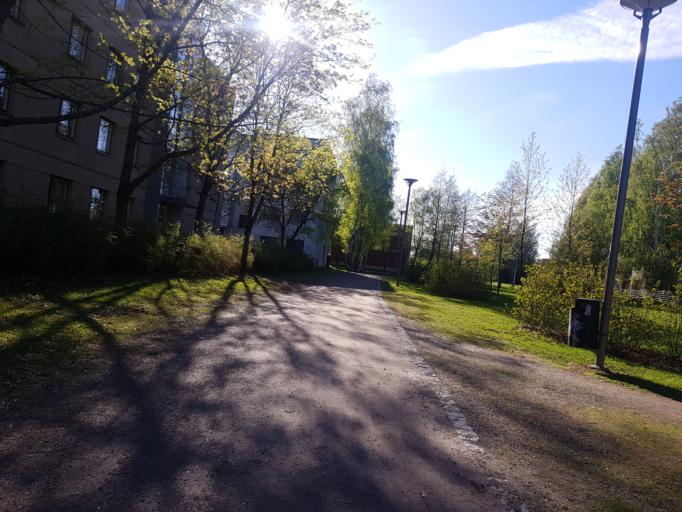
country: FI
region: Uusimaa
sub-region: Helsinki
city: Vantaa
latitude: 60.2745
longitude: 25.0310
